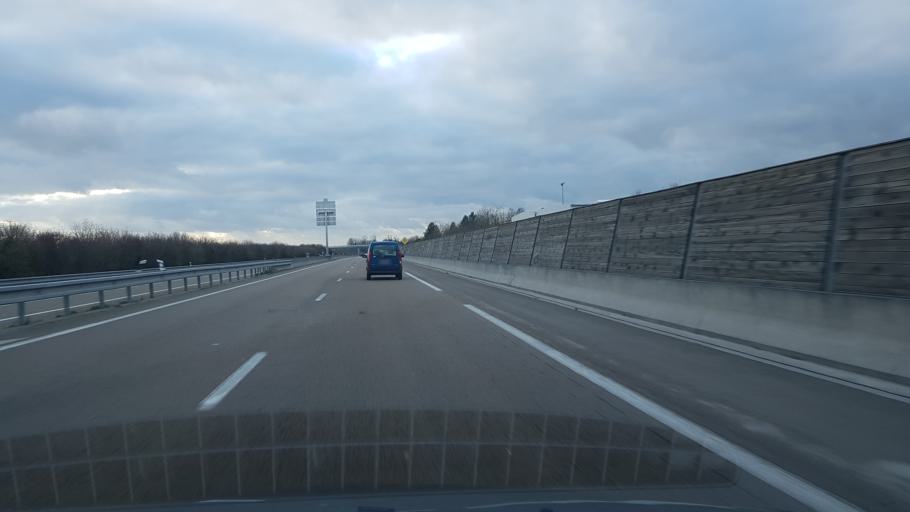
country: FR
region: Champagne-Ardenne
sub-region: Departement de la Marne
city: Fere-Champenoise
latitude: 48.7492
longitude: 3.9945
